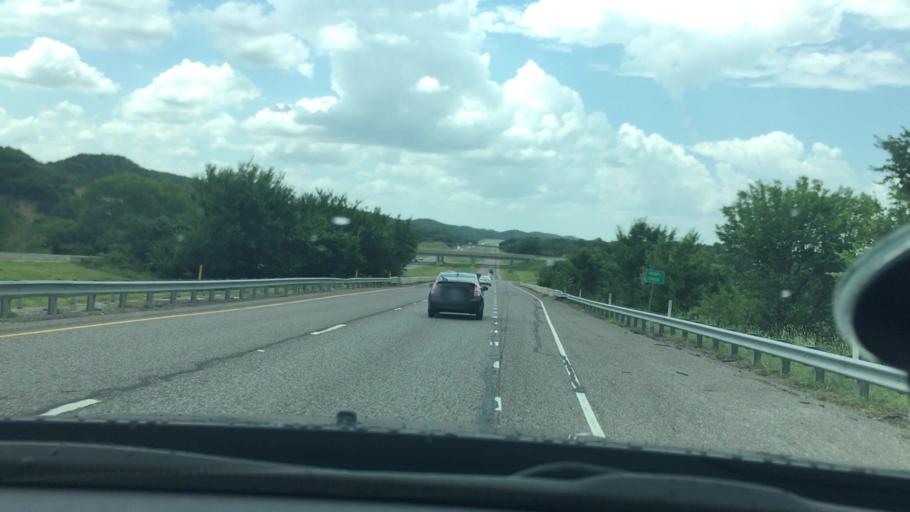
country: US
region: Oklahoma
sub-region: Murray County
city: Davis
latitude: 34.4467
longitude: -97.1312
